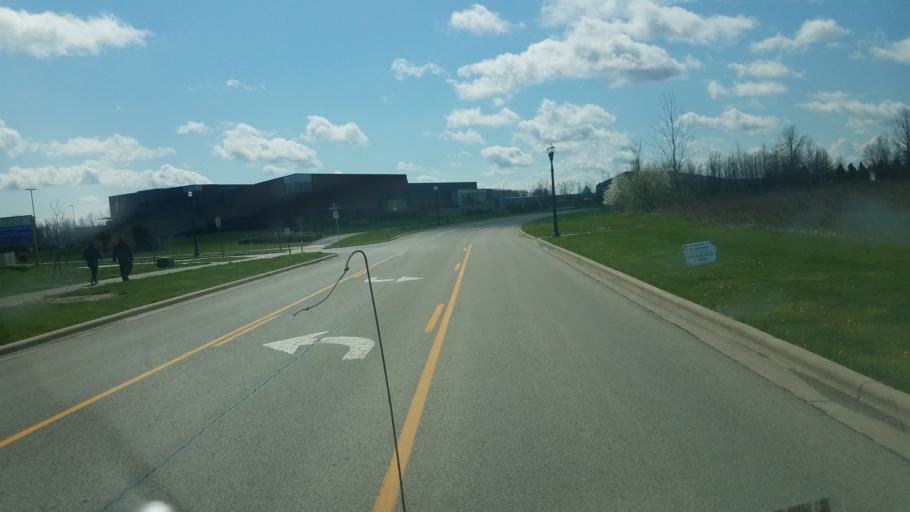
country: US
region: Ohio
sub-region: Delaware County
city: Delaware
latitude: 40.2897
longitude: -83.1140
